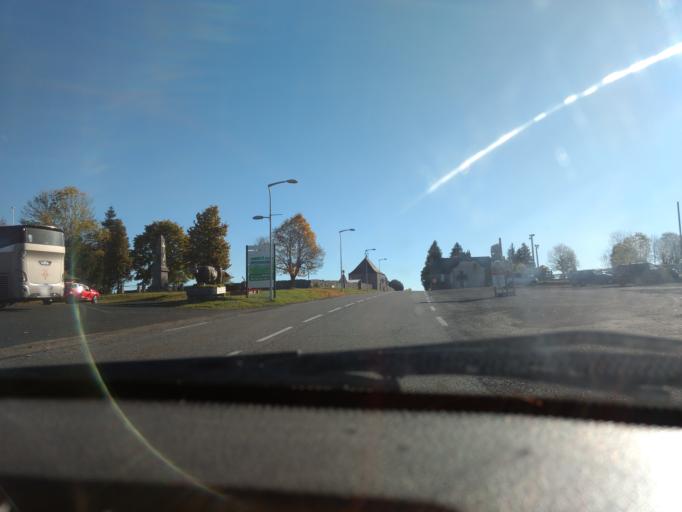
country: FR
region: Midi-Pyrenees
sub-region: Departement de l'Aveyron
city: Laguiole
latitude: 44.7727
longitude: 2.8838
